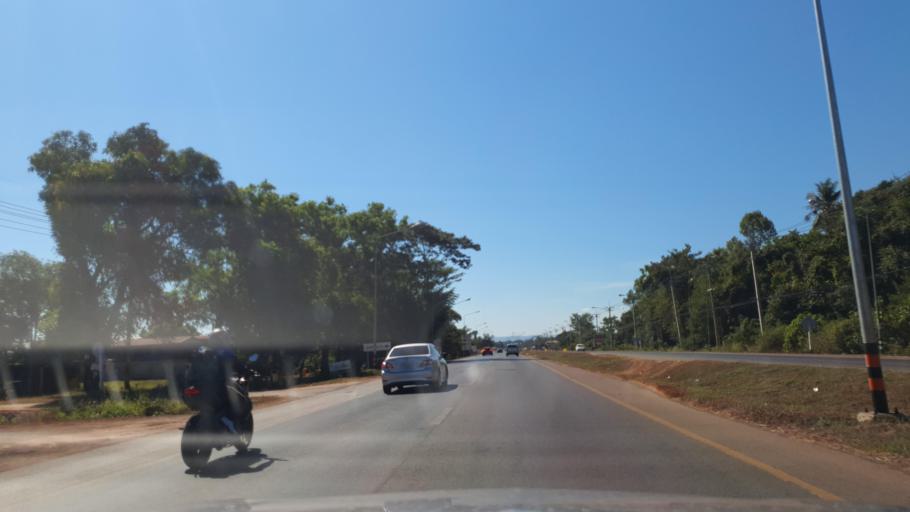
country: TH
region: Sakon Nakhon
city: Sakon Nakhon
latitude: 17.2205
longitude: 104.1049
